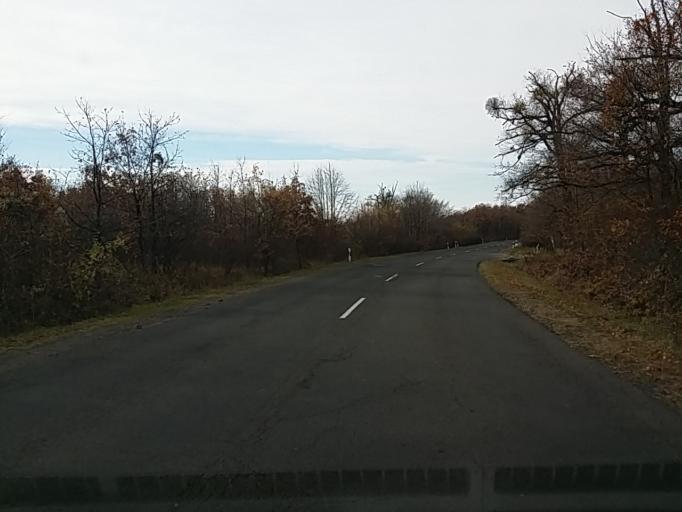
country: HU
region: Heves
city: Gyongyossolymos
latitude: 47.8519
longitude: 19.9682
